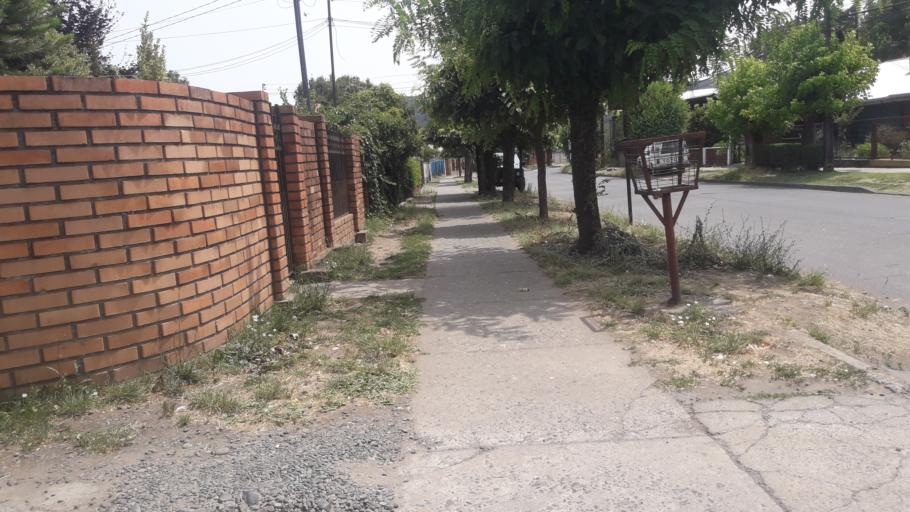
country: CL
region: Biobio
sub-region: Provincia de Biobio
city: Nacimiento
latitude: -37.5047
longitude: -72.6811
